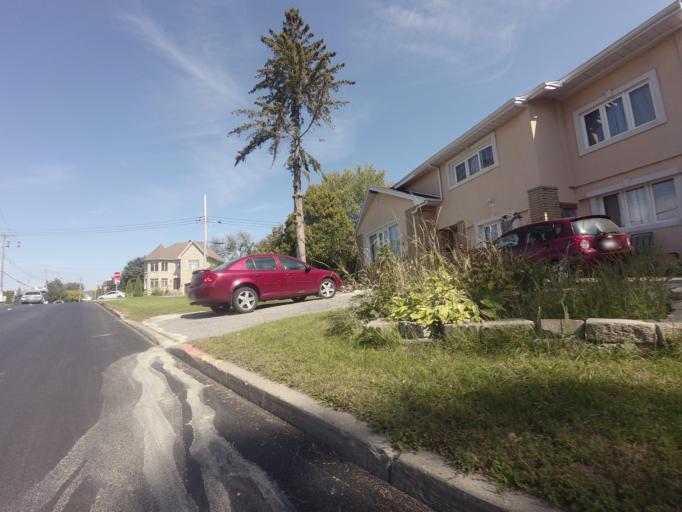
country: CA
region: Quebec
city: Dollard-Des Ormeaux
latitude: 45.5048
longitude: -73.8611
